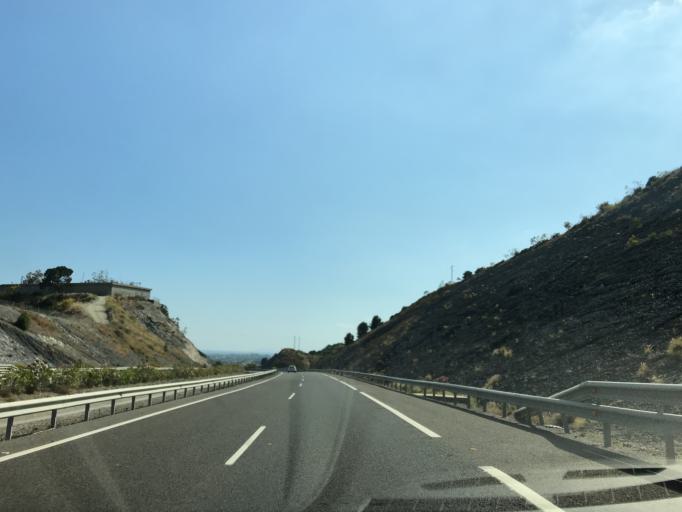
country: ES
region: Andalusia
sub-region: Provincia de Malaga
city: Benahavis
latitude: 36.5221
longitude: -4.9792
